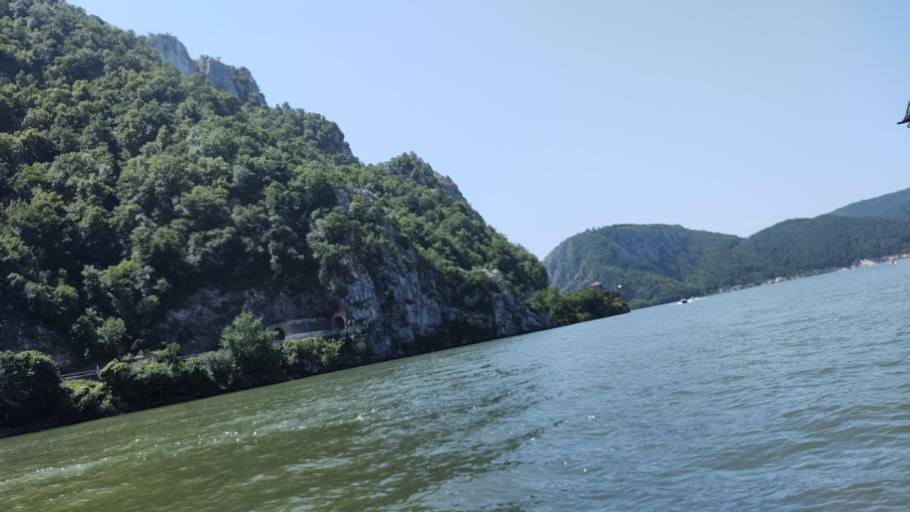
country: RO
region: Mehedinti
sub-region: Comuna Dubova
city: Dubova
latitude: 44.6286
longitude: 22.2821
